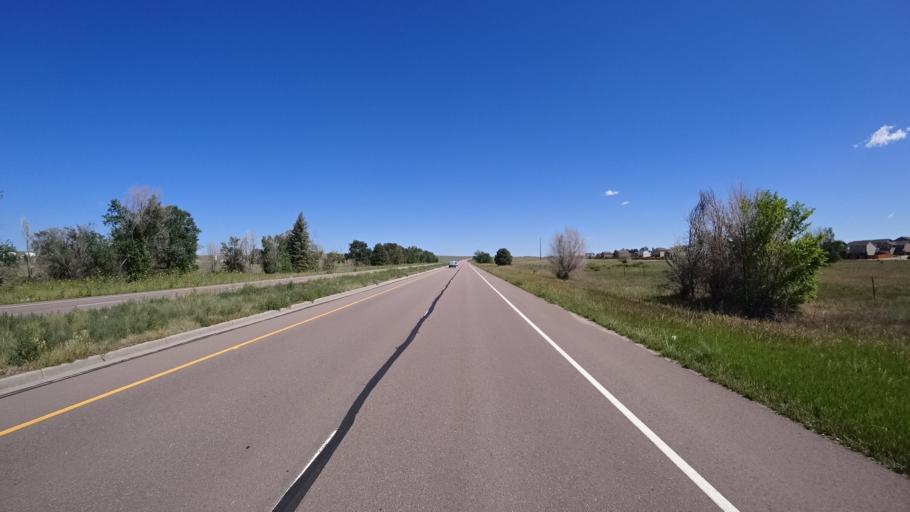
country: US
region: Colorado
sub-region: El Paso County
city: Security-Widefield
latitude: 38.7757
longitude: -104.6596
